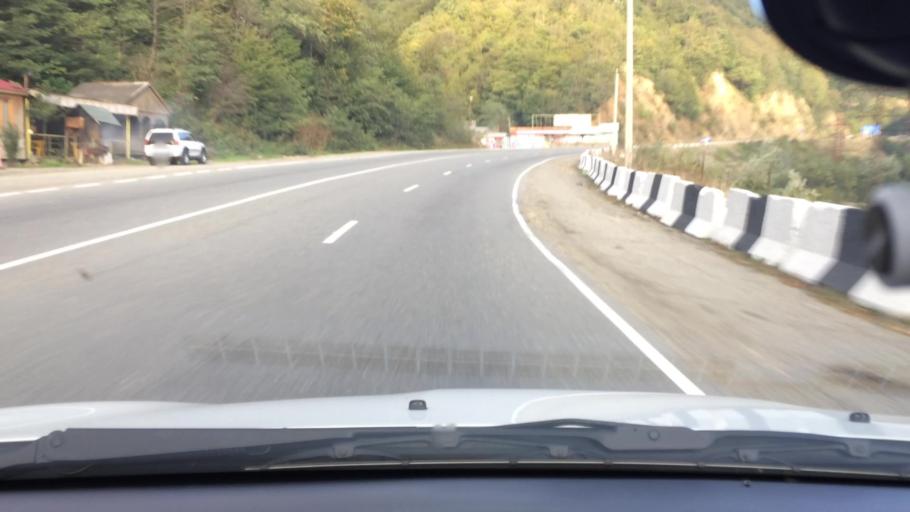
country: GE
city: Surami
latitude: 42.0419
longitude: 43.5021
